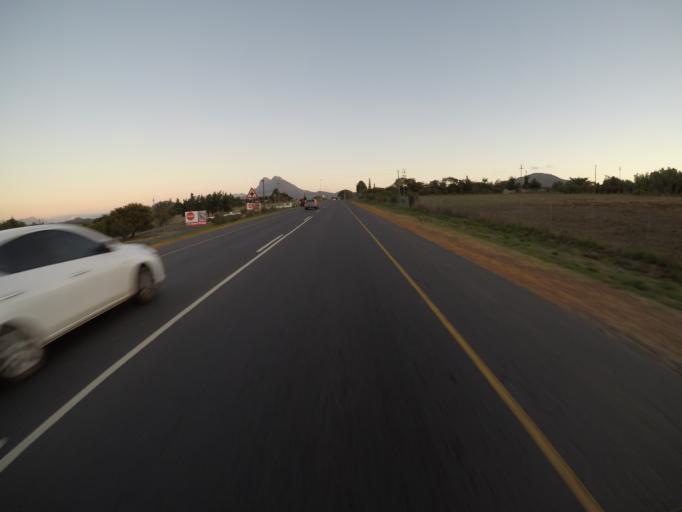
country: ZA
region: Western Cape
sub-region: Cape Winelands District Municipality
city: Paarl
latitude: -33.8005
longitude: 18.8713
